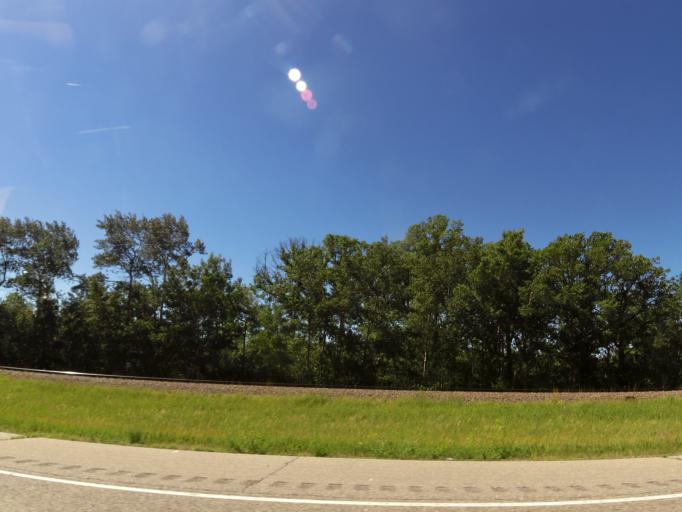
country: US
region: Minnesota
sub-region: Red Lake County
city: Red Lake Falls
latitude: 47.6937
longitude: -96.1058
